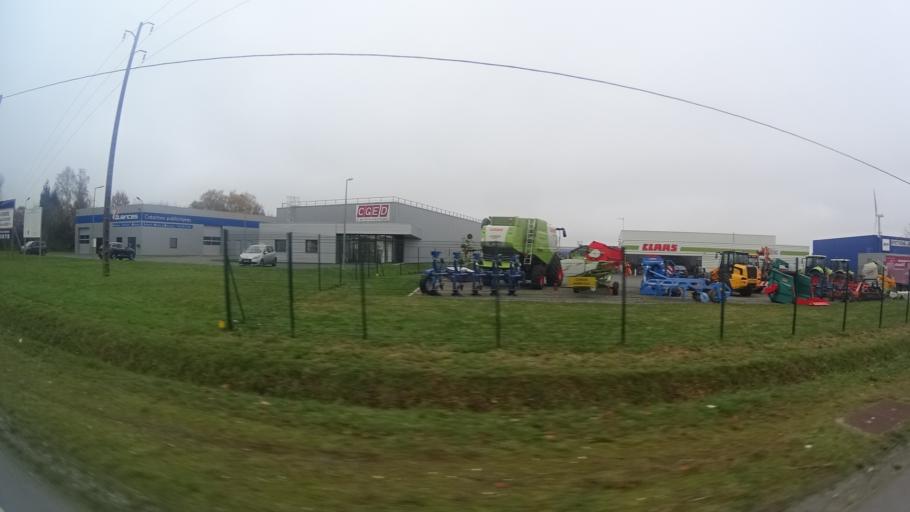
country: FR
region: Brittany
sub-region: Departement d'Ille-et-Vilaine
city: Bains-sur-Oust
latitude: 47.6860
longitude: -2.0547
